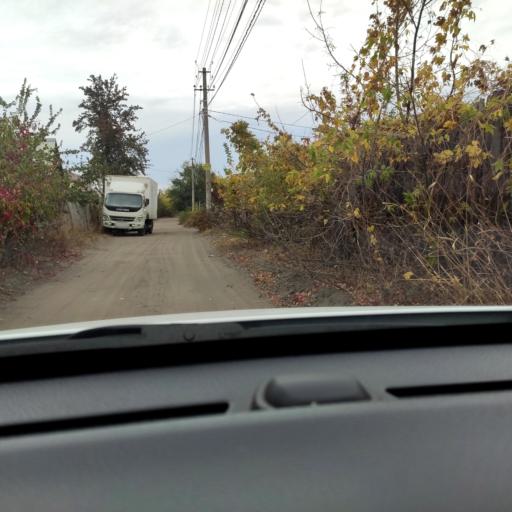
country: RU
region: Voronezj
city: Maslovka
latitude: 51.6045
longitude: 39.2782
